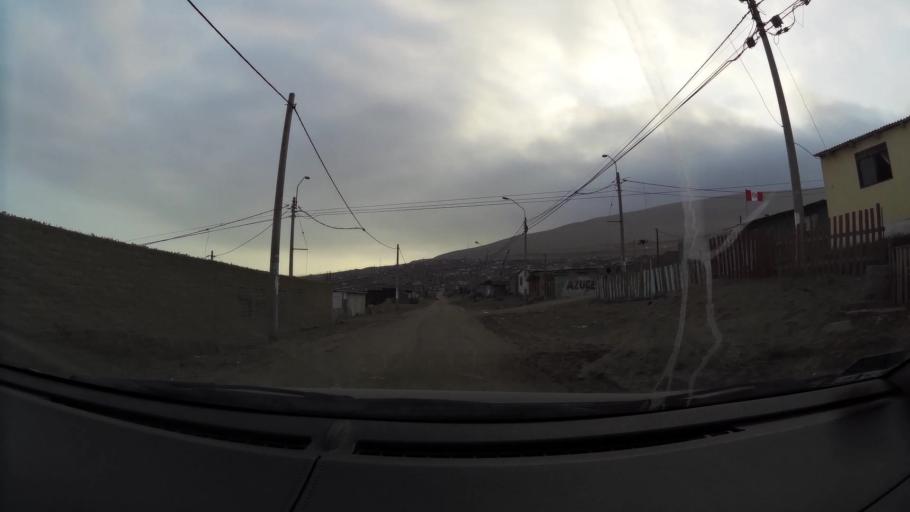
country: PE
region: Lima
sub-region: Lima
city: Santa Rosa
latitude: -11.7295
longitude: -77.1415
